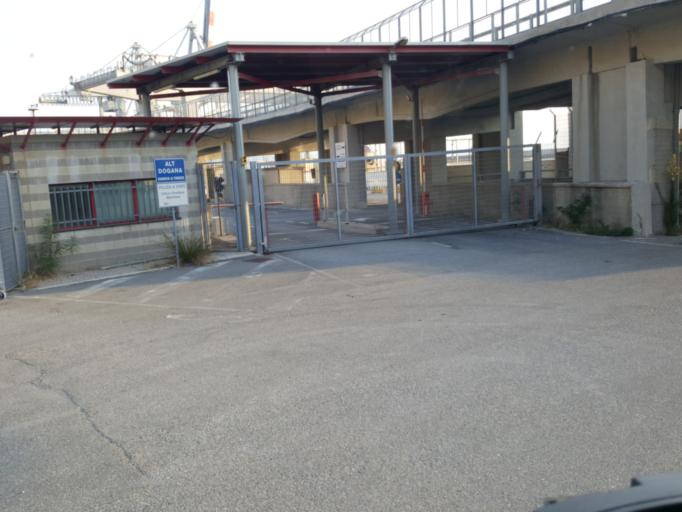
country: IT
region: Liguria
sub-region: Provincia di Savona
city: Bergeggi
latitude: 44.2590
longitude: 8.4526
